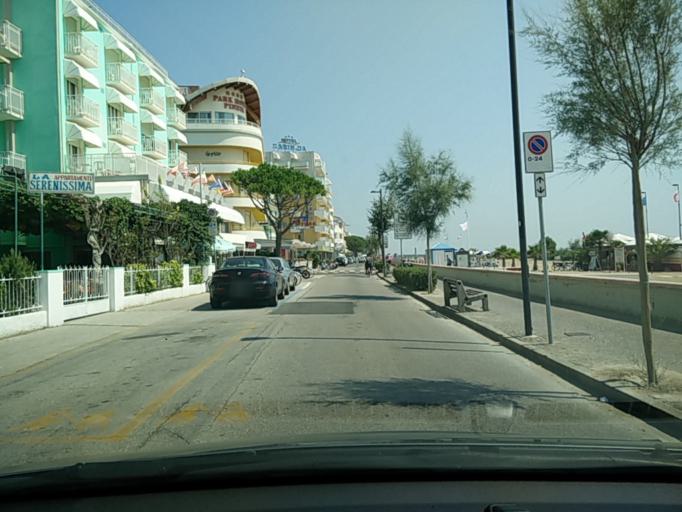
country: IT
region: Veneto
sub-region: Provincia di Venezia
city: Caorle
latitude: 45.6054
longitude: 12.8917
